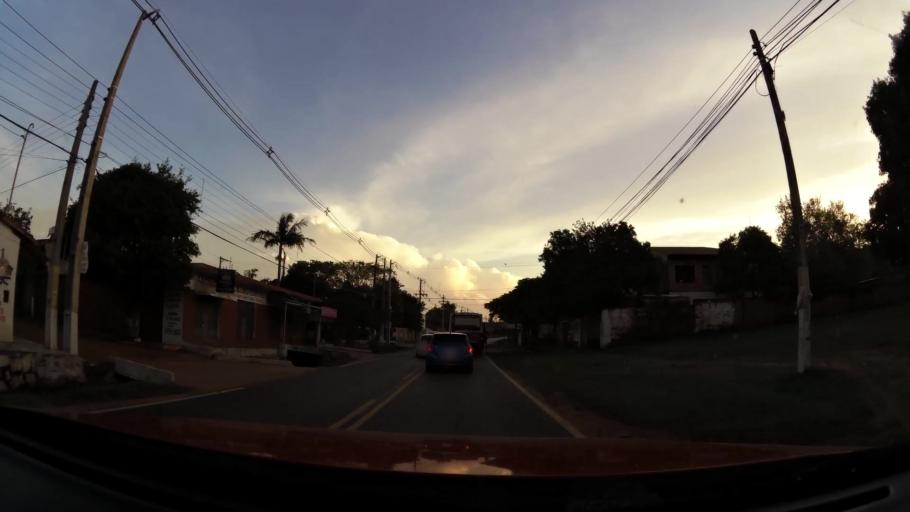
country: PY
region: Central
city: San Lorenzo
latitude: -25.3783
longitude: -57.4929
